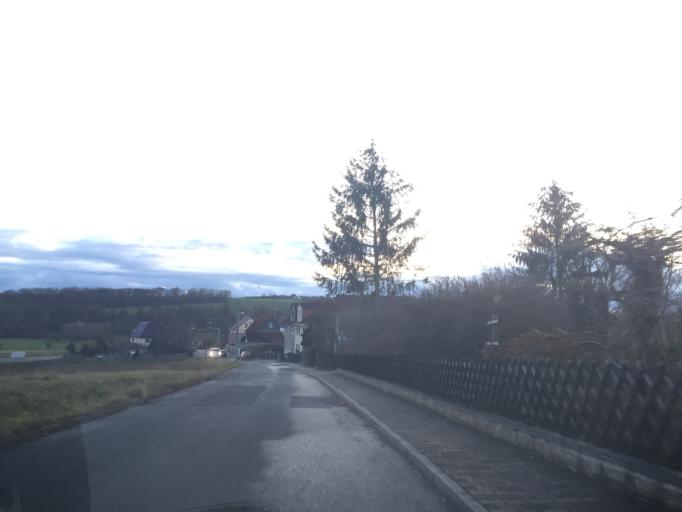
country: DE
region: Thuringia
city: Schmolln
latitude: 50.8943
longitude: 12.3301
